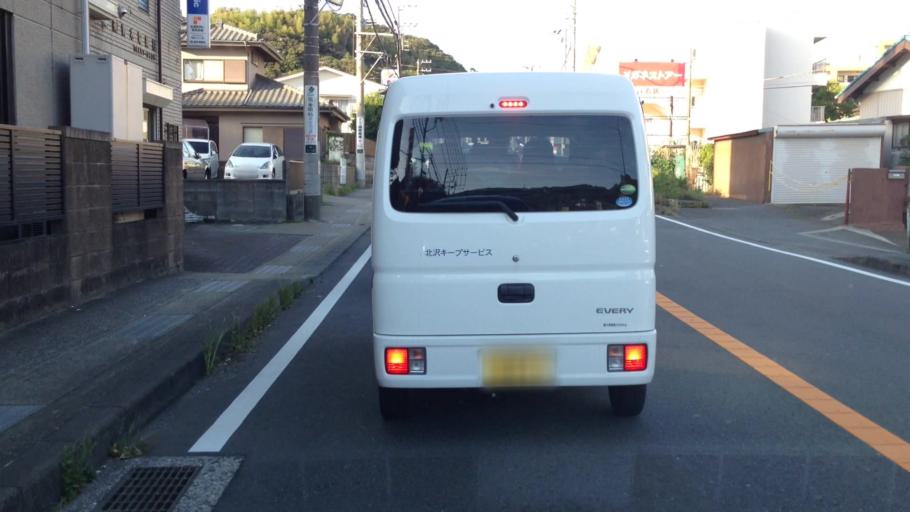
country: JP
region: Kanagawa
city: Yokosuka
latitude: 35.2286
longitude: 139.6518
